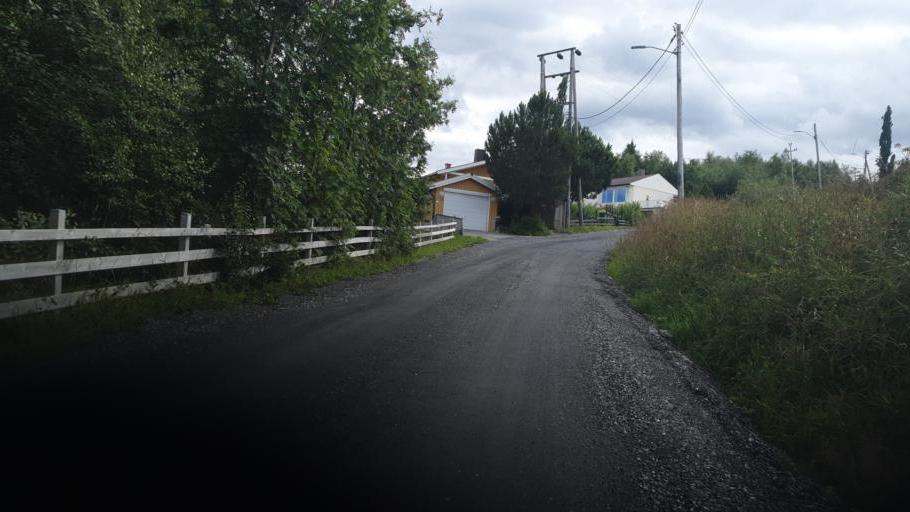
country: NO
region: Sor-Trondelag
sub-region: Malvik
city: Malvik
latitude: 63.4328
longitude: 10.6904
